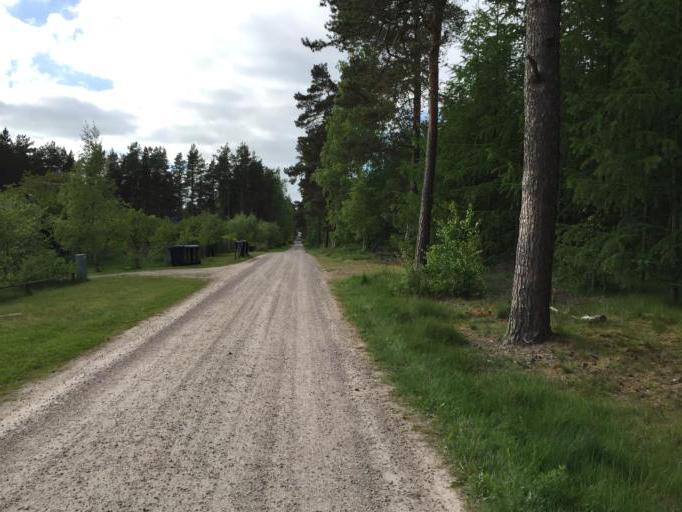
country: SE
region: Skane
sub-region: Sjobo Kommun
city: Sjoebo
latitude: 55.6660
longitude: 13.6348
